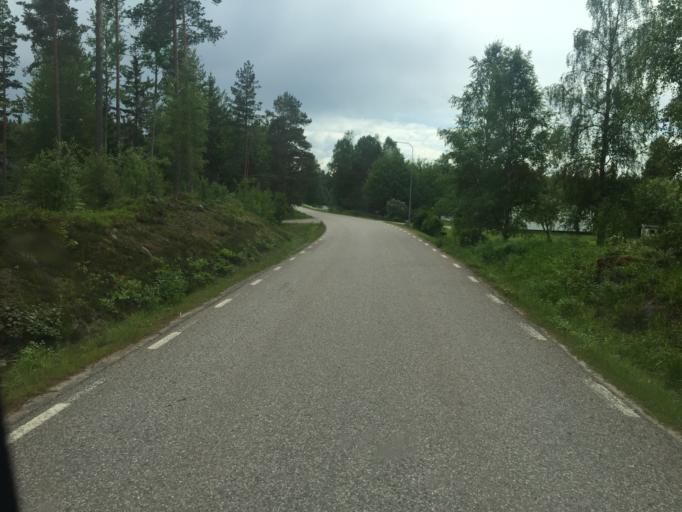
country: SE
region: Dalarna
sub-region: Vansbro Kommun
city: Vansbro
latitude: 60.4778
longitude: 14.0042
